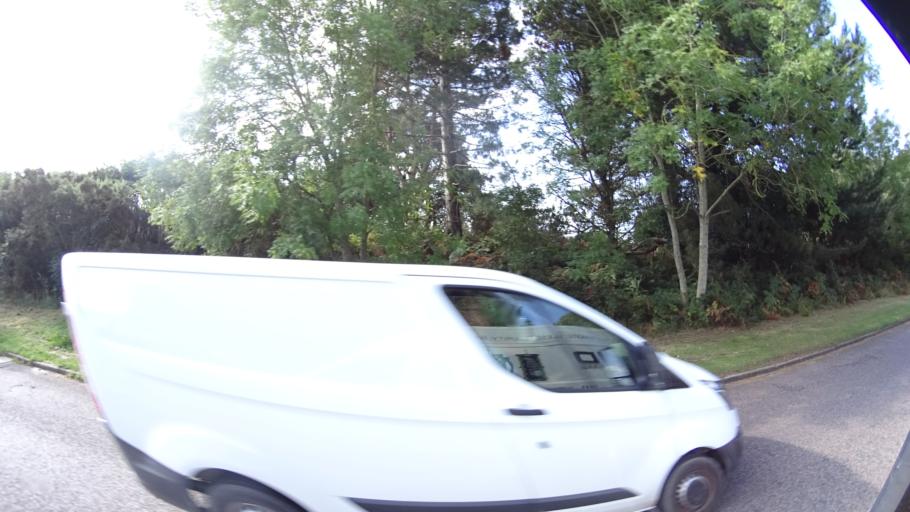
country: GB
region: England
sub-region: Dorset
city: Parkstone
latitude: 50.7538
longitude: -1.9157
